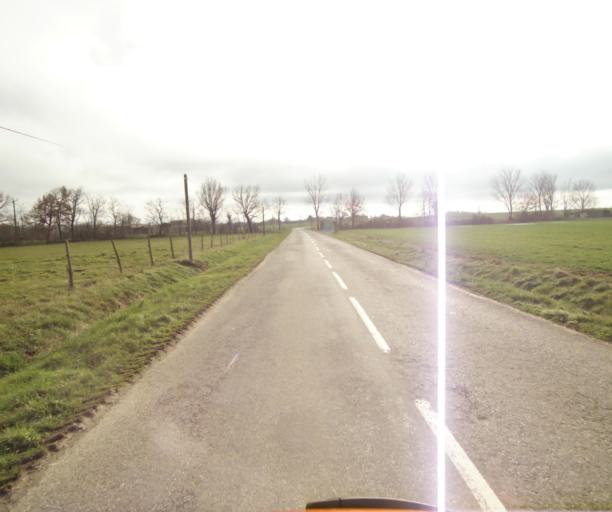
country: FR
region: Languedoc-Roussillon
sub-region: Departement de l'Aude
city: Belpech
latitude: 43.1939
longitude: 1.7293
